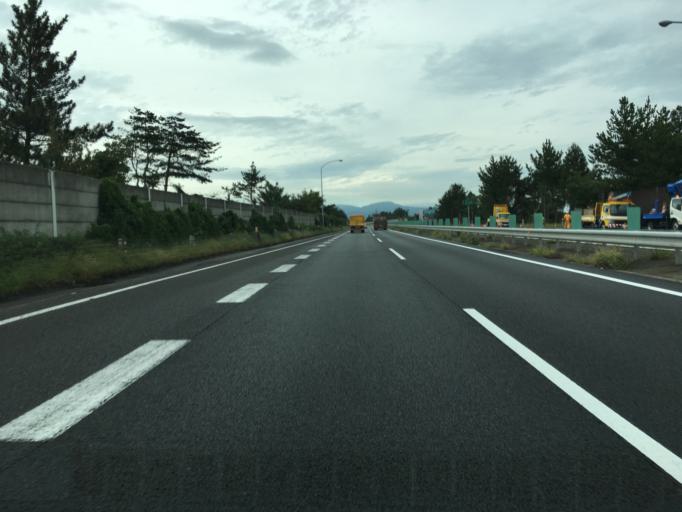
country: JP
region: Fukushima
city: Fukushima-shi
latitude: 37.7625
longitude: 140.4095
